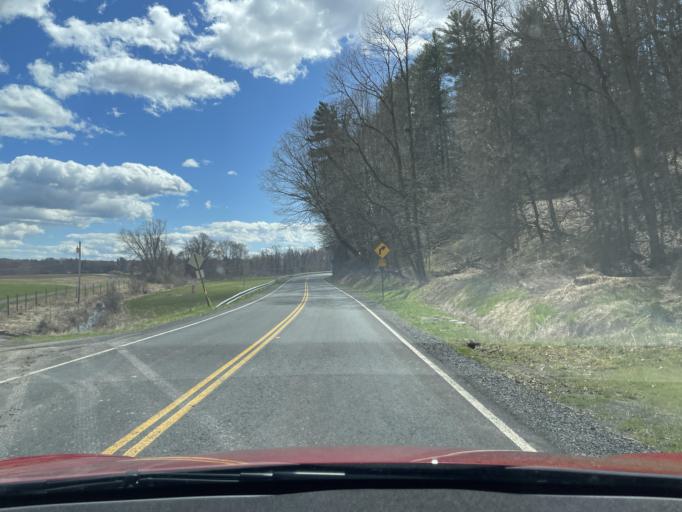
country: US
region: New York
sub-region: Ulster County
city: Hurley
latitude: 41.9385
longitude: -74.0711
